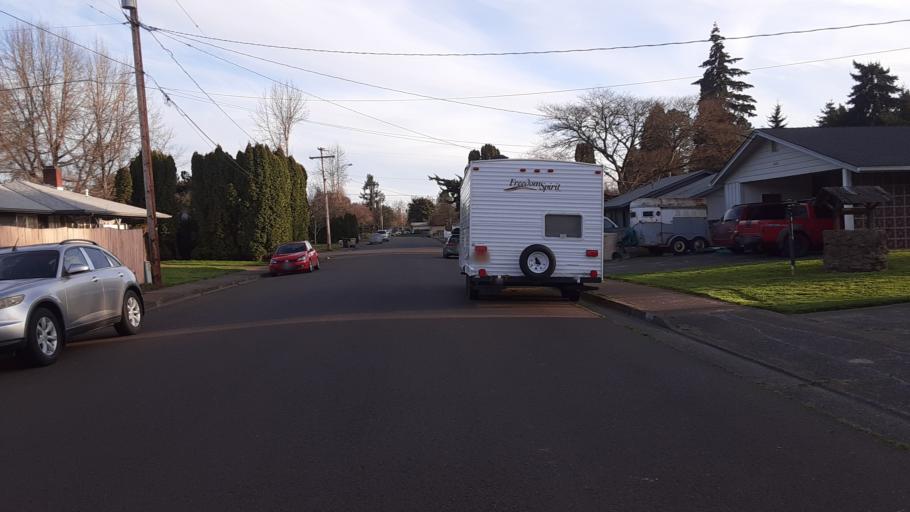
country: US
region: Oregon
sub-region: Benton County
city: Corvallis
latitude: 44.5423
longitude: -123.2586
